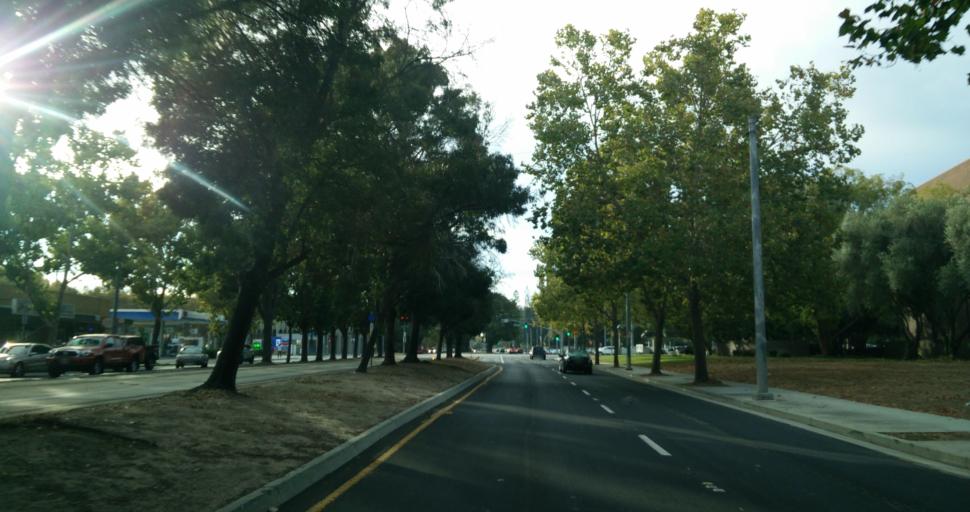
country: US
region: California
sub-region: Santa Clara County
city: San Jose
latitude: 37.3562
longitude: -121.9057
